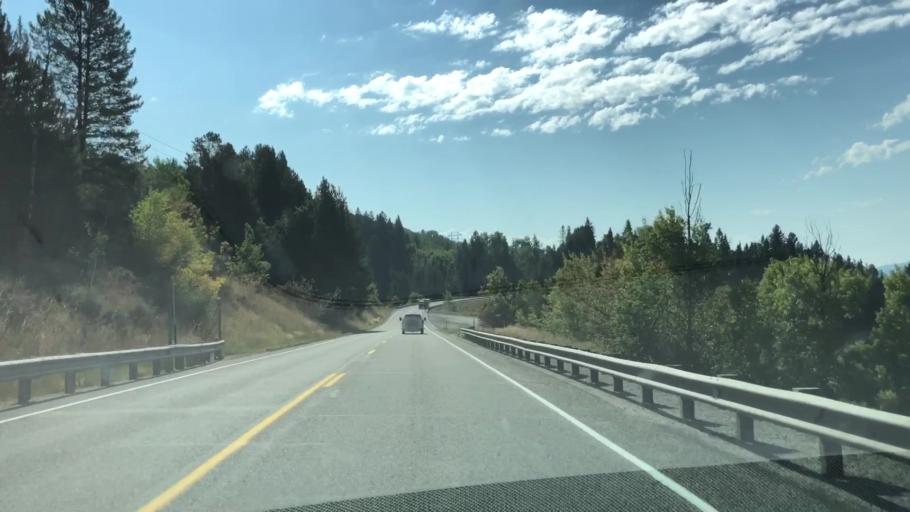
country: US
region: Idaho
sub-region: Teton County
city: Victor
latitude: 43.3019
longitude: -111.1320
